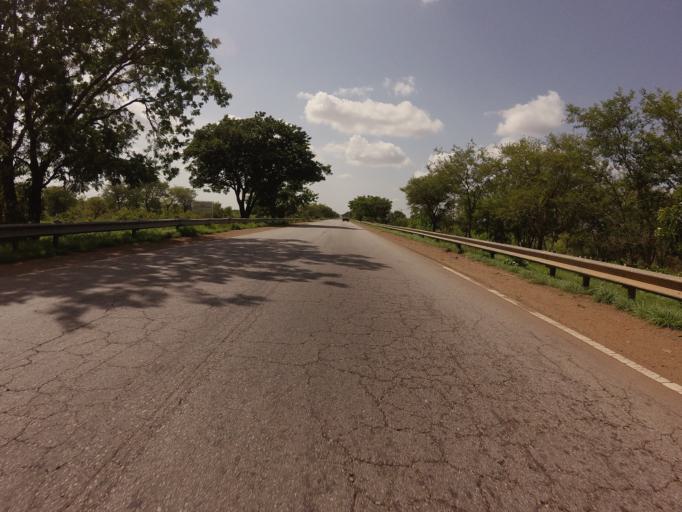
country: GH
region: Northern
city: Savelugu
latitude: 9.8303
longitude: -0.8648
